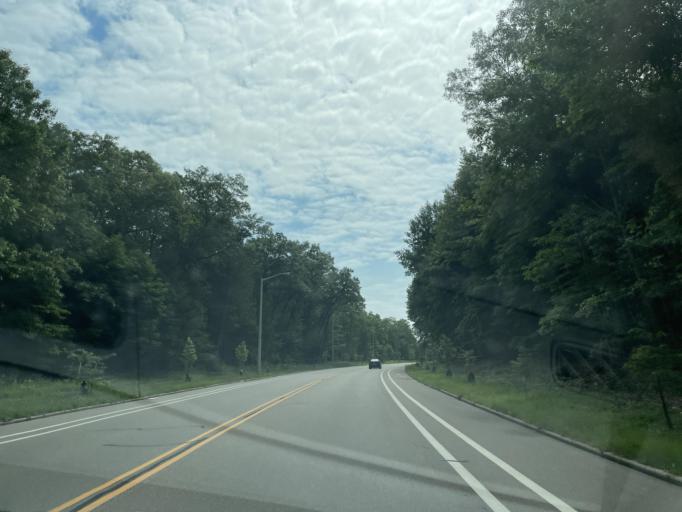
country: US
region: Michigan
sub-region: Kent County
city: East Grand Rapids
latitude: 42.9197
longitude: -85.6286
